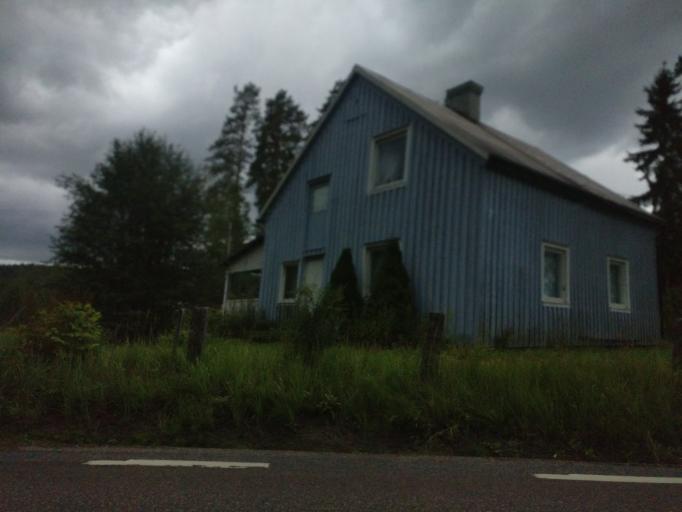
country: SE
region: Vaermland
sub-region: Torsby Kommun
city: Torsby
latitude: 60.6311
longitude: 13.0201
